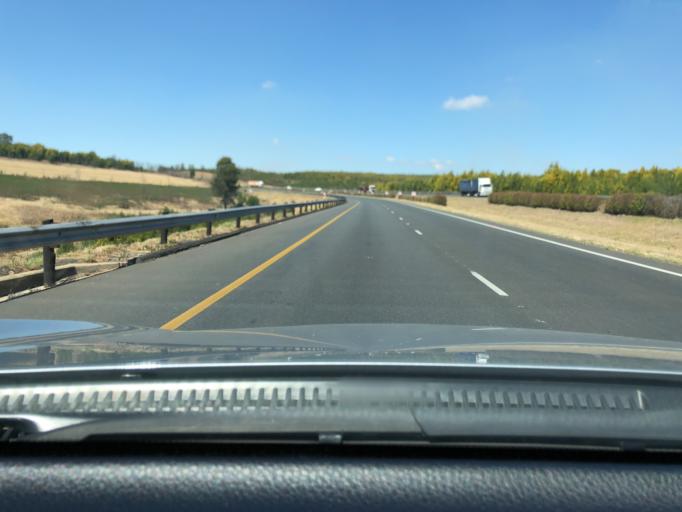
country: ZA
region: KwaZulu-Natal
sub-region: uMgungundlovu District Municipality
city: Mooirivier
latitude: -29.1206
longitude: 29.9482
